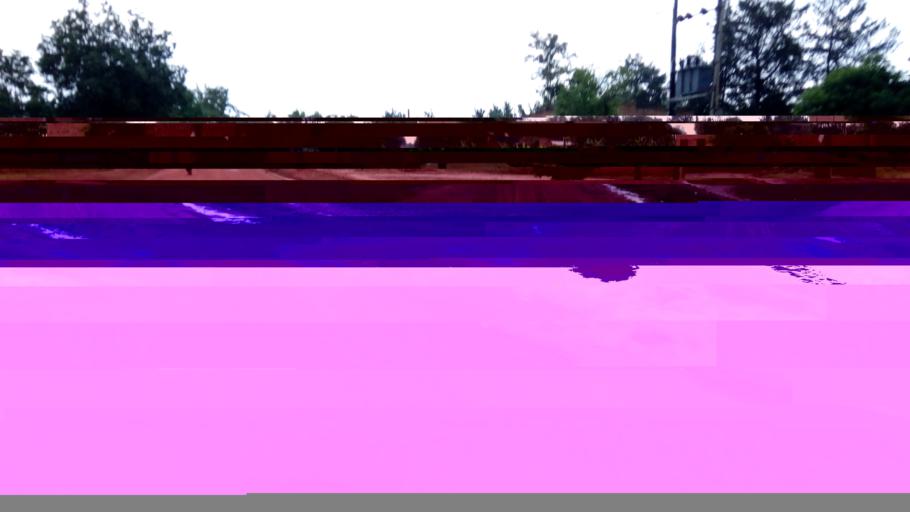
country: UG
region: Eastern Region
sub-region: Mbale District
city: Mbale
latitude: 1.0787
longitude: 34.0947
